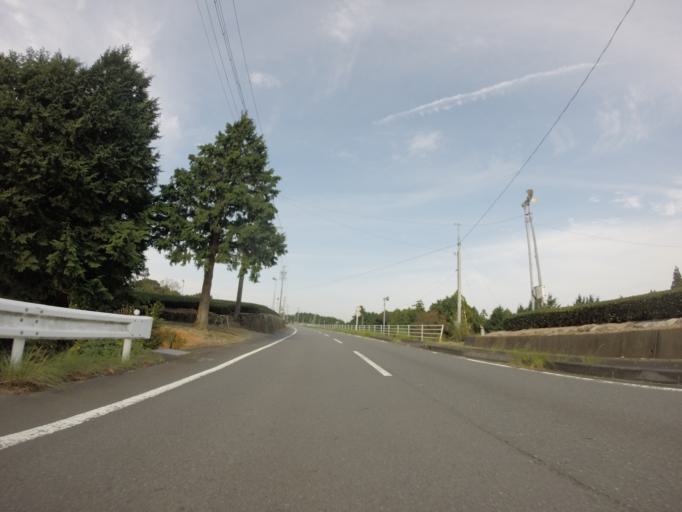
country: JP
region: Shizuoka
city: Shimada
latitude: 34.7712
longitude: 138.1649
